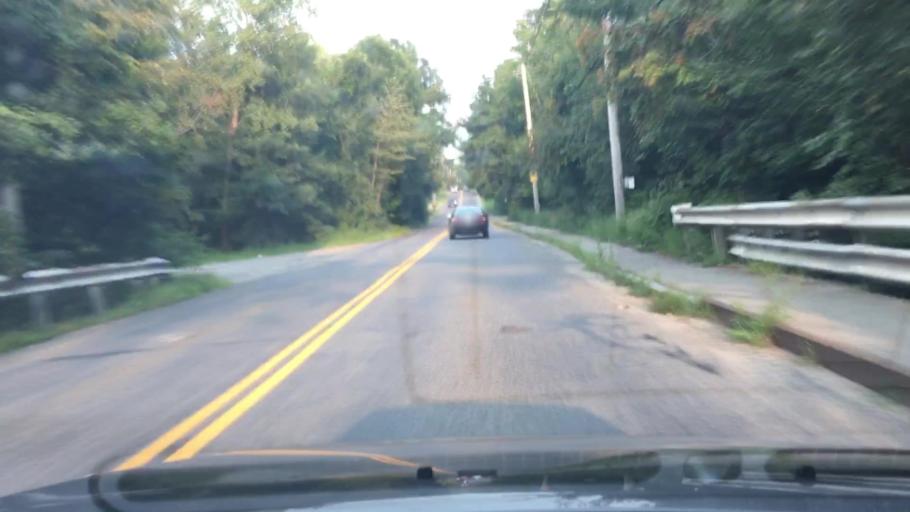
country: US
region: Massachusetts
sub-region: Worcester County
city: Westborough
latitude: 42.2712
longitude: -71.6327
